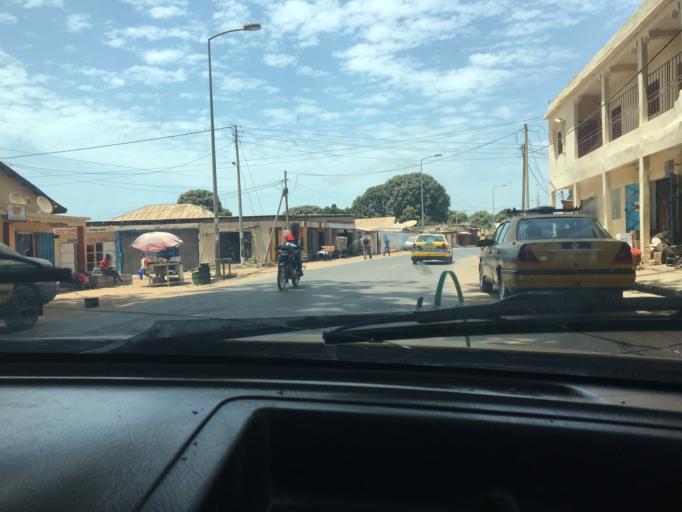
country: GM
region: Banjul
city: Bakau
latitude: 13.4491
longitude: -16.6845
